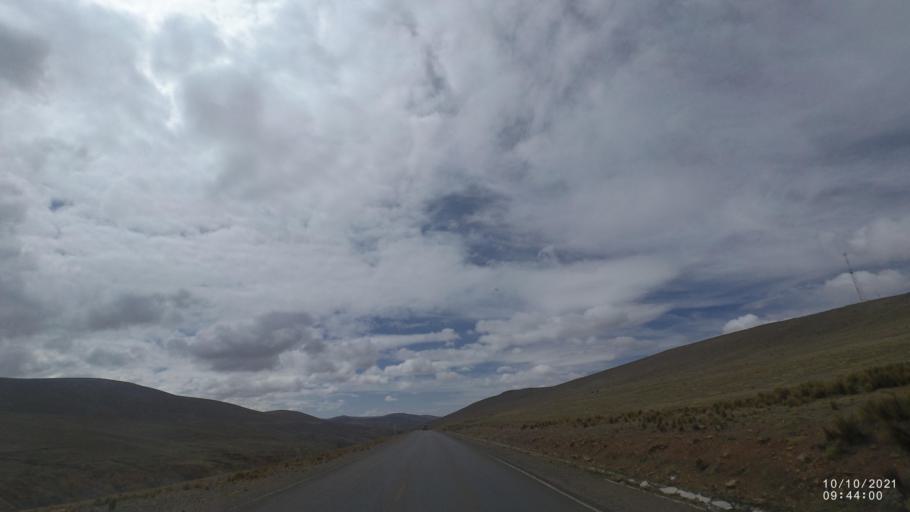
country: BO
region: La Paz
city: Quime
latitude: -17.1559
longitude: -67.3422
